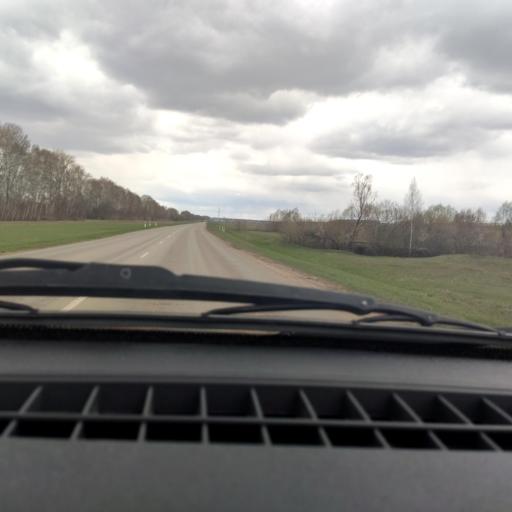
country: RU
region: Bashkortostan
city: Chekmagush
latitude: 55.1207
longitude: 54.7378
